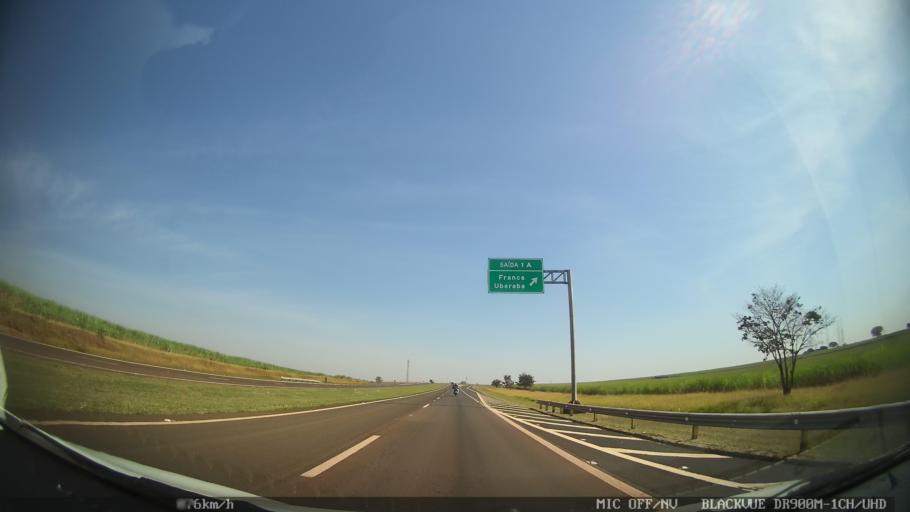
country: BR
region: Sao Paulo
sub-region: Ribeirao Preto
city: Ribeirao Preto
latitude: -21.1663
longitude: -47.8935
